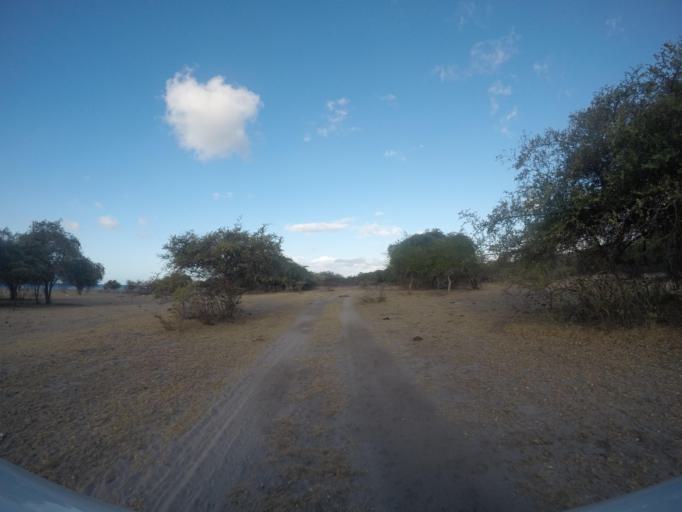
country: TL
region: Lautem
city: Lospalos
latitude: -8.3247
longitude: 126.9884
